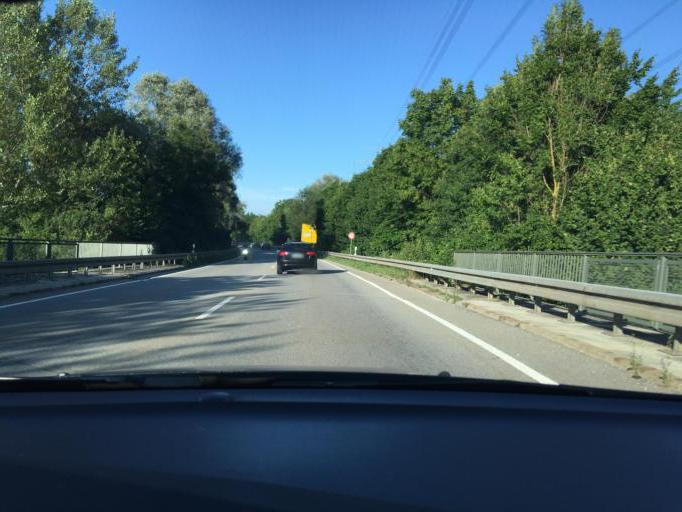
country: DE
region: Bavaria
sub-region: Upper Bavaria
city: Unterfoehring
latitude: 48.1784
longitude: 11.6520
